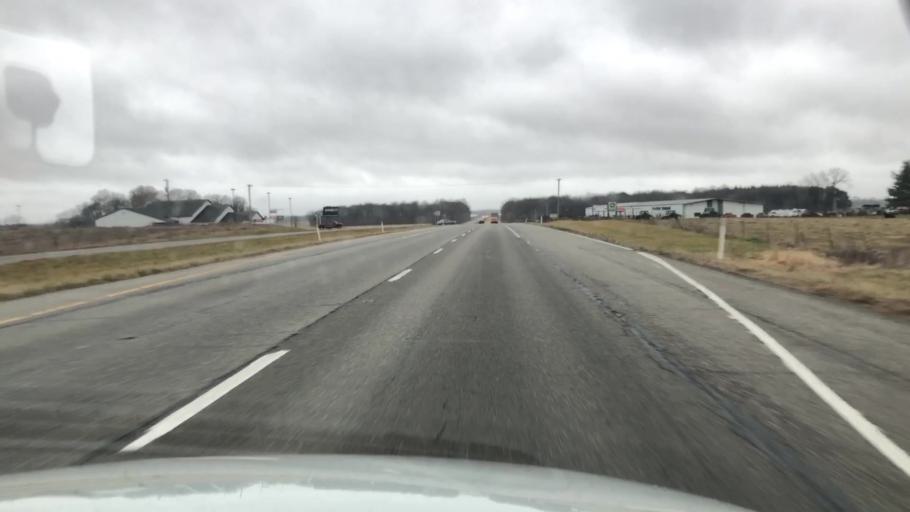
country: US
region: Indiana
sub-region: Marshall County
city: Argos
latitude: 41.3279
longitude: -86.2196
